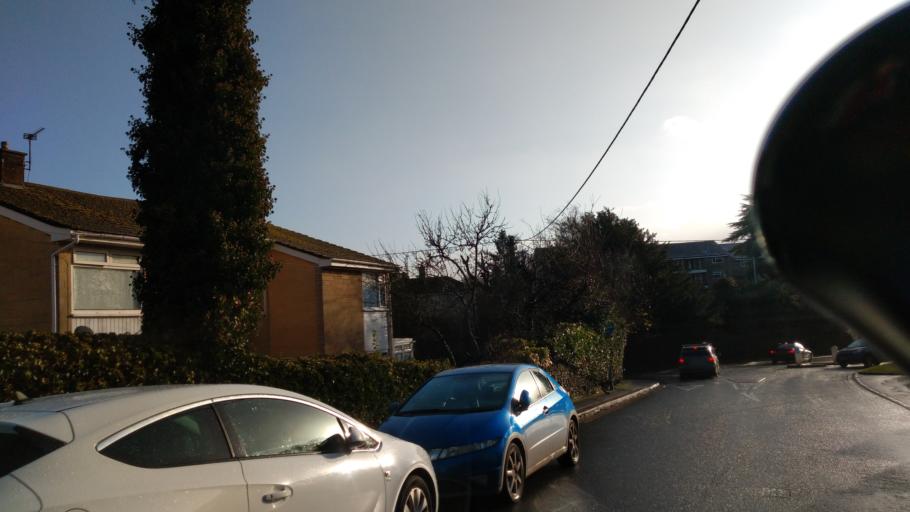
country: GB
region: England
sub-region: Wiltshire
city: Bradford-on-Avon
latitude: 51.3495
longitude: -2.2431
